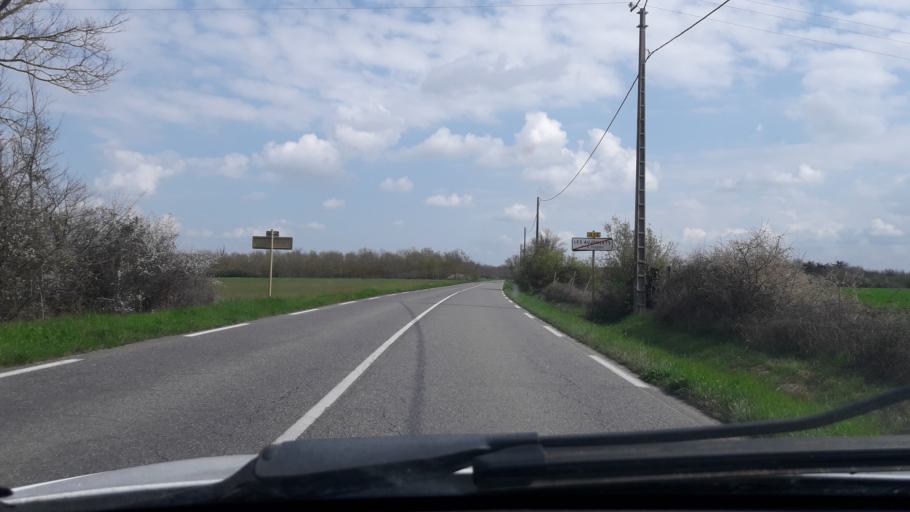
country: FR
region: Midi-Pyrenees
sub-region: Departement de la Haute-Garonne
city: Fonsorbes
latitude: 43.5032
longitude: 1.2630
